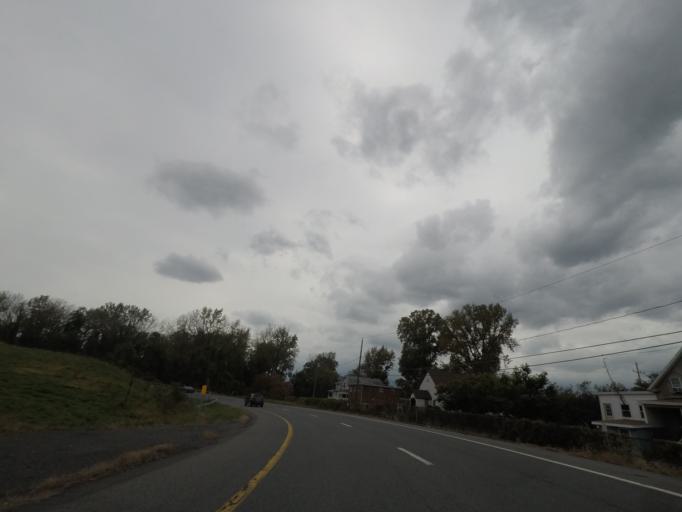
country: US
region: New York
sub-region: Albany County
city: Roessleville
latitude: 42.6881
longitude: -73.8023
